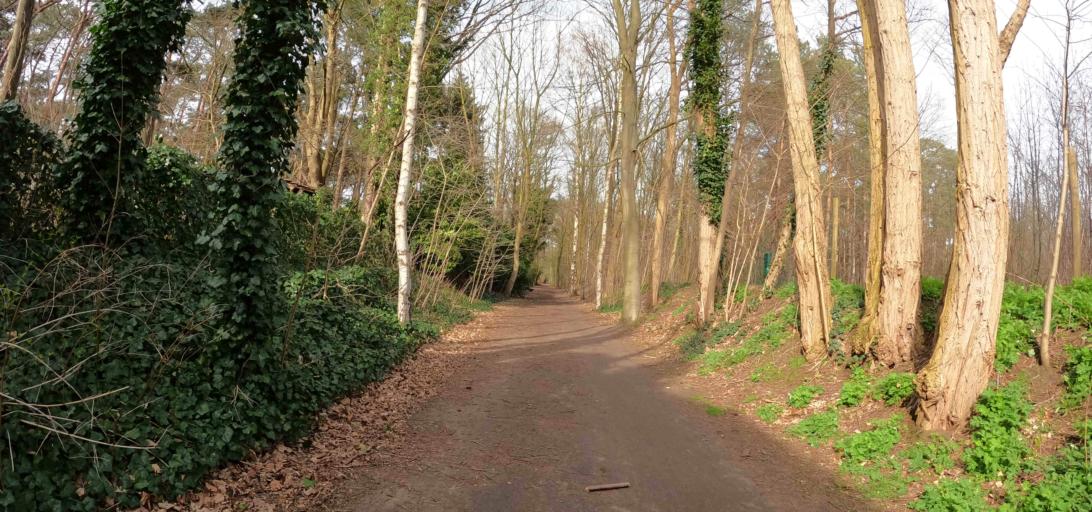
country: BE
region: Flanders
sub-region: Provincie Oost-Vlaanderen
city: Waasmunster
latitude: 51.1228
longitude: 4.0903
